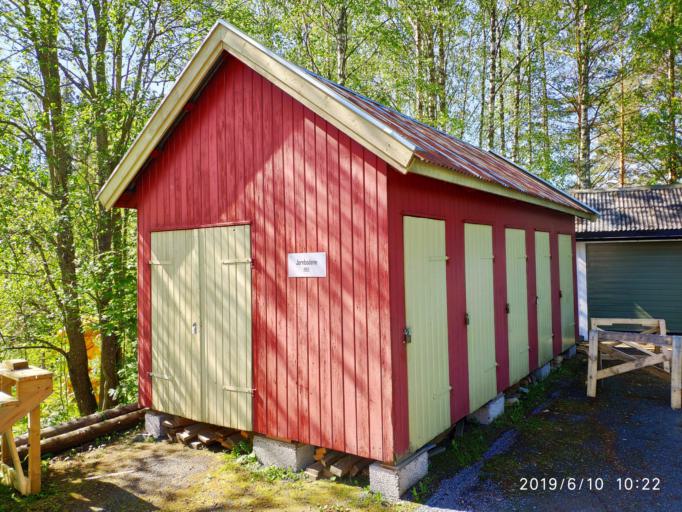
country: NO
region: Oppland
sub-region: Jevnaker
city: Jevnaker
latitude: 60.2215
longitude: 10.3685
